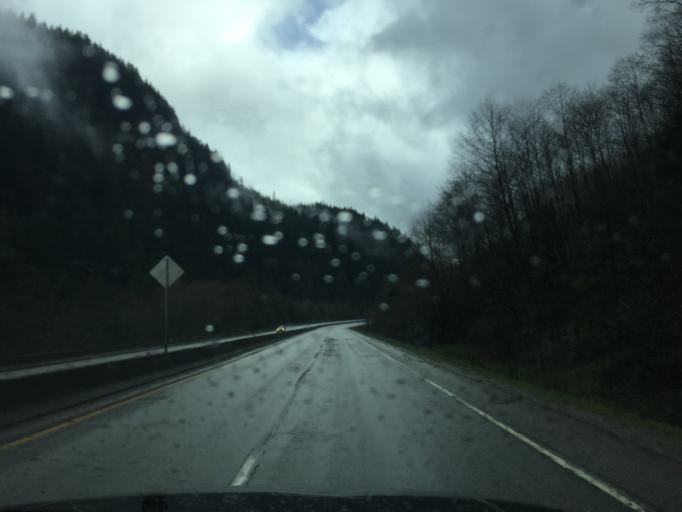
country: CA
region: British Columbia
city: Hope
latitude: 49.4266
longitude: -121.3116
